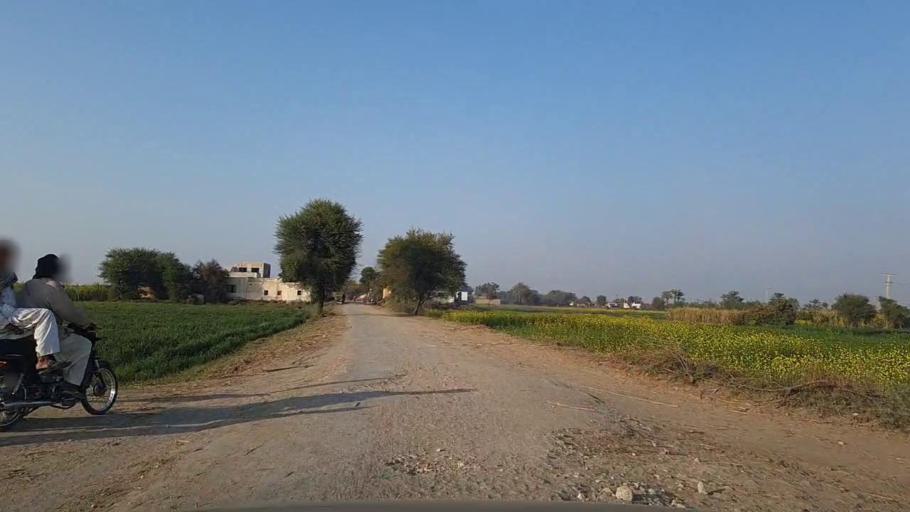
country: PK
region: Sindh
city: Tando Mittha Khan
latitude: 25.9439
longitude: 69.0764
